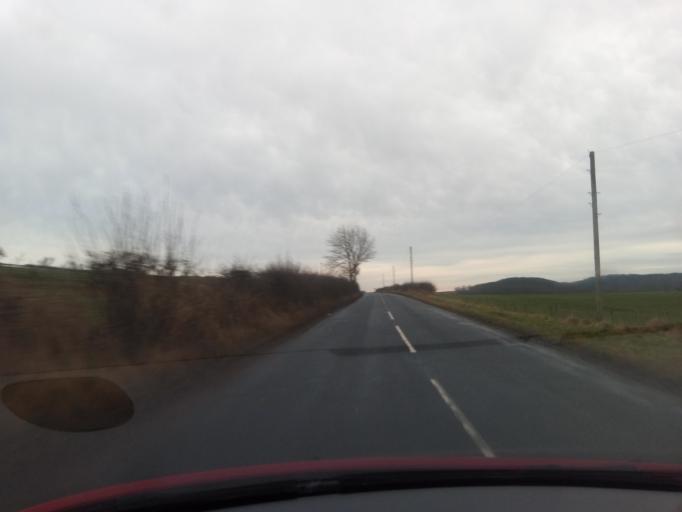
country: GB
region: England
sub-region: Northumberland
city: Ellingham
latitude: 55.4585
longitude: -1.7726
